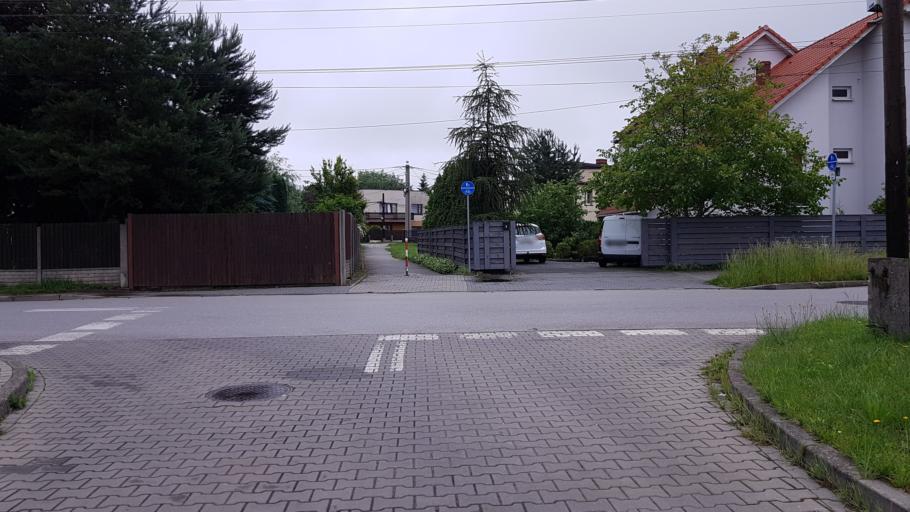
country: PL
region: Silesian Voivodeship
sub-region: Tychy
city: Tychy
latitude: 50.1085
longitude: 18.9612
